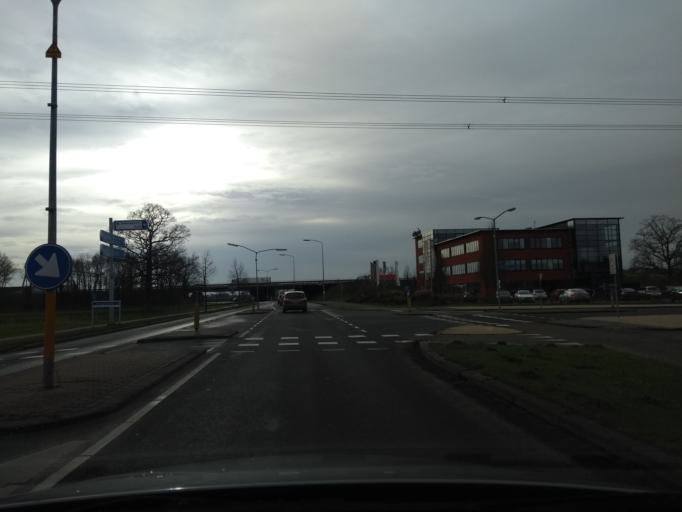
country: NL
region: Overijssel
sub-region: Gemeente Almelo
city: Almelo
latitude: 52.3245
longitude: 6.6537
